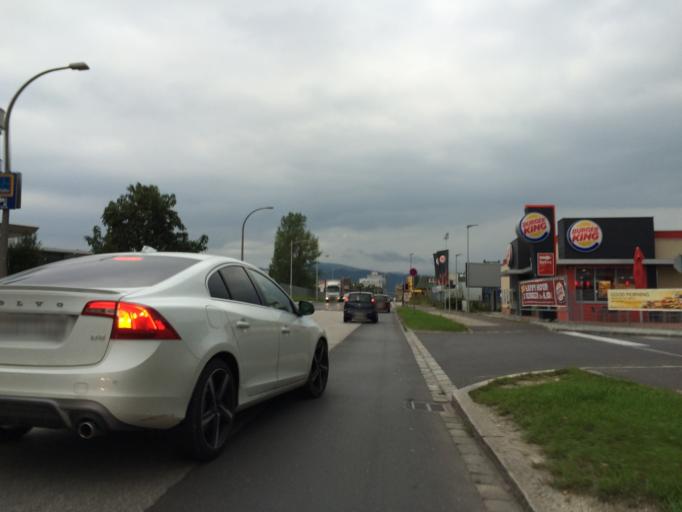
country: AT
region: Upper Austria
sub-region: Linz Stadt
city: Linz
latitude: 48.3080
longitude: 14.3156
